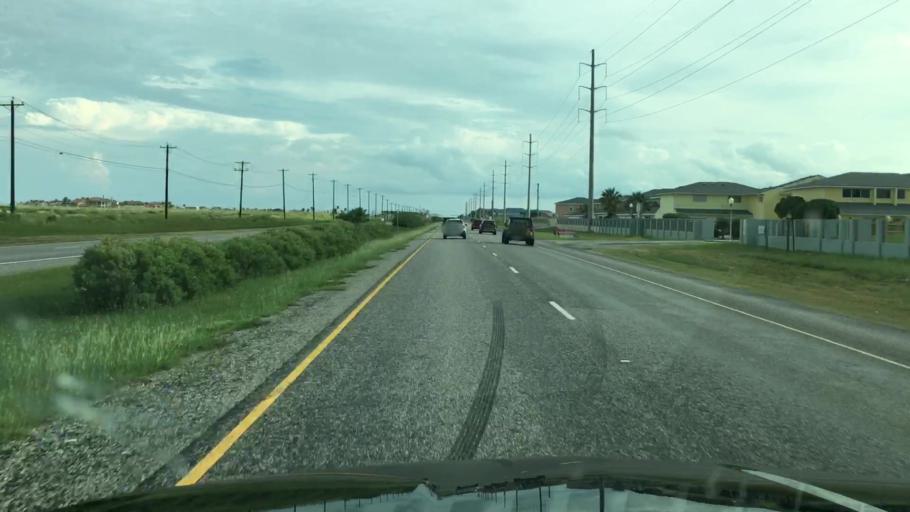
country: US
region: Texas
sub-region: Nueces County
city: Corpus Christi
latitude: 27.6135
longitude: -97.2219
